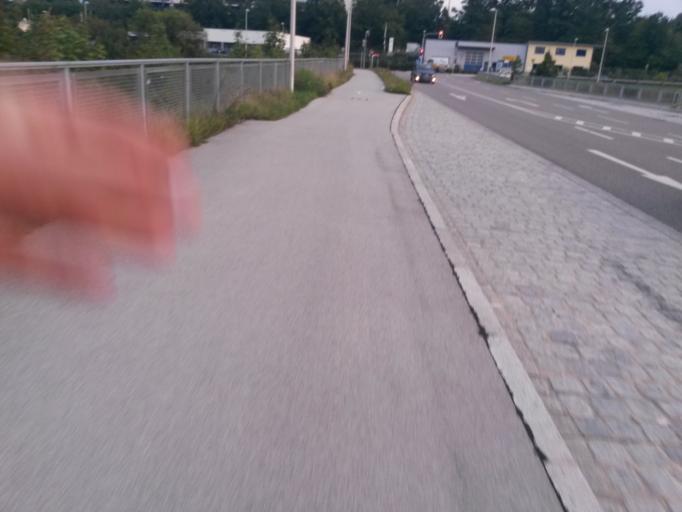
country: DE
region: Bavaria
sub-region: Regierungsbezirk Mittelfranken
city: Zirndorf
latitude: 49.4342
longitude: 10.9417
